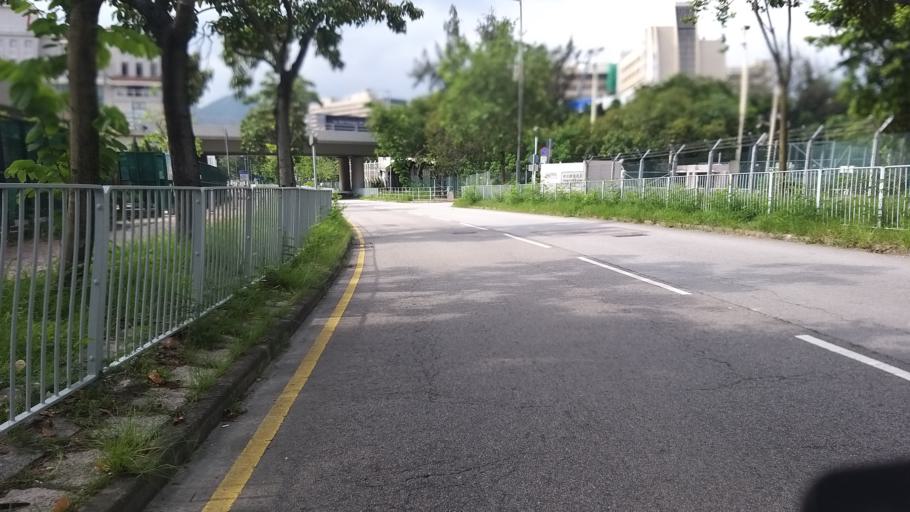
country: HK
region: Tuen Mun
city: Tuen Mun
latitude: 22.4047
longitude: 113.9749
